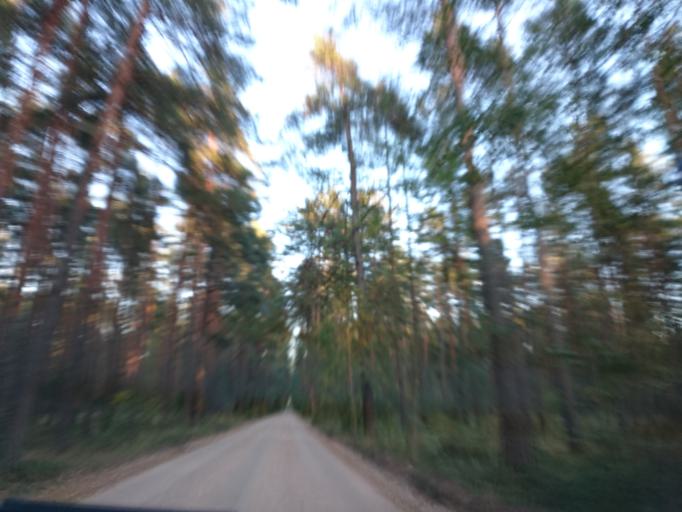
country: LV
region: Adazi
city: Adazi
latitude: 57.0523
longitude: 24.3124
